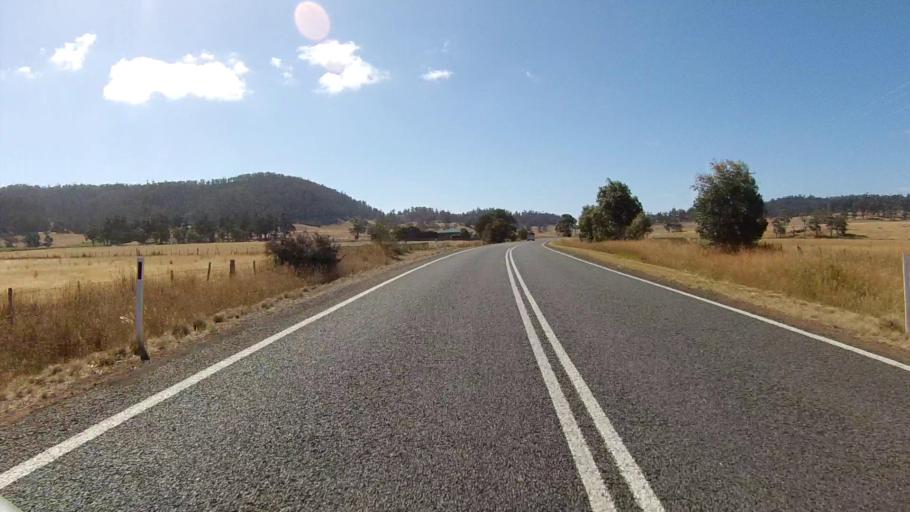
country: AU
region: Tasmania
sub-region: Sorell
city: Sorell
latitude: -42.4422
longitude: 147.9279
